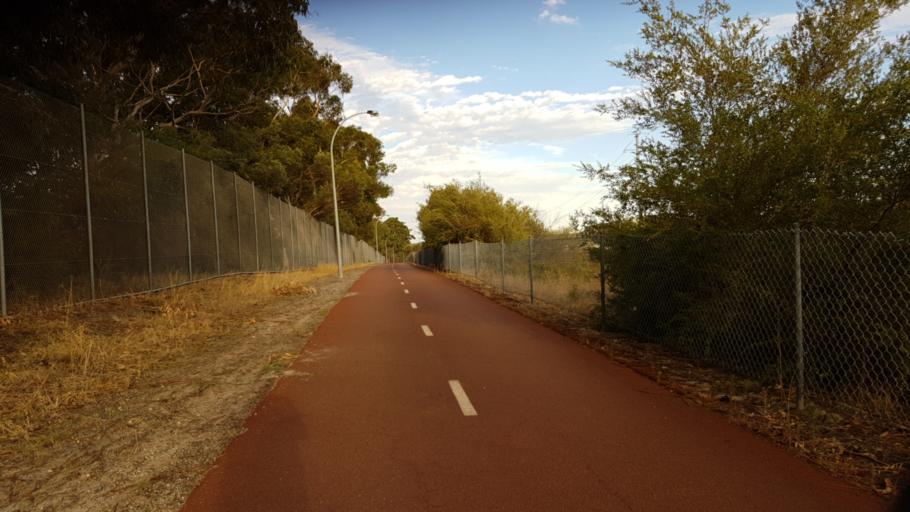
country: AU
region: Western Australia
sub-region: Canning
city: Canning Vale
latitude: -32.0542
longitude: 115.9146
